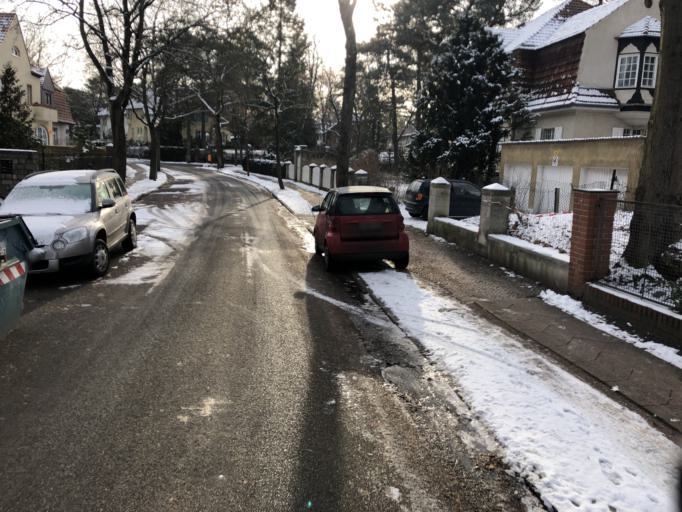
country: DE
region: Berlin
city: Hermsdorf
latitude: 52.6208
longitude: 13.3097
